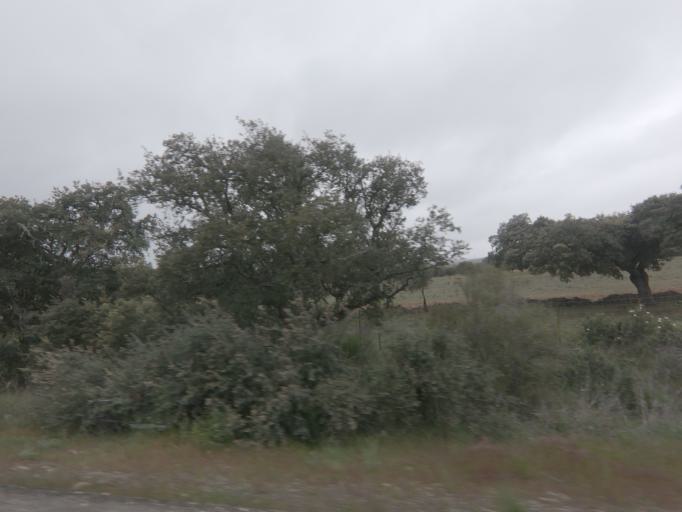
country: ES
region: Extremadura
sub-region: Provincia de Caceres
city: Malpartida de Caceres
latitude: 39.2942
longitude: -6.5203
